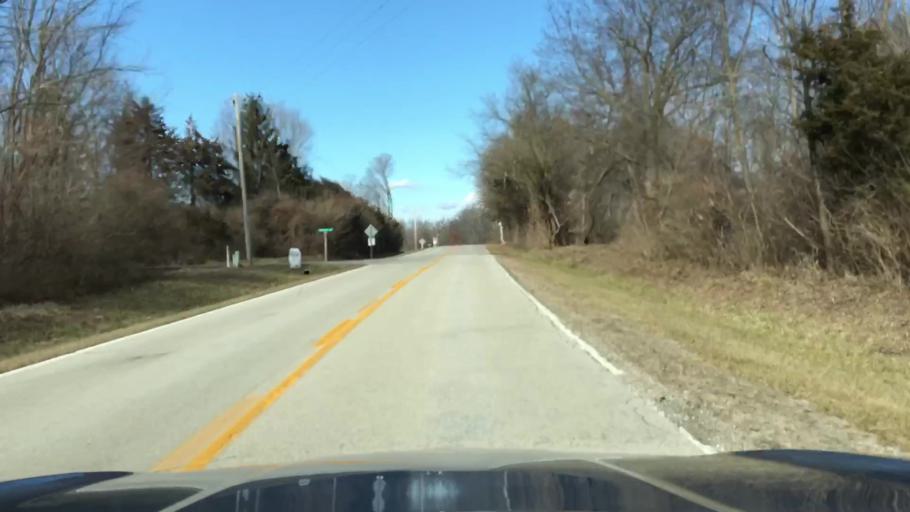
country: US
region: Illinois
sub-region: McLean County
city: Hudson
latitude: 40.6557
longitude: -88.9242
